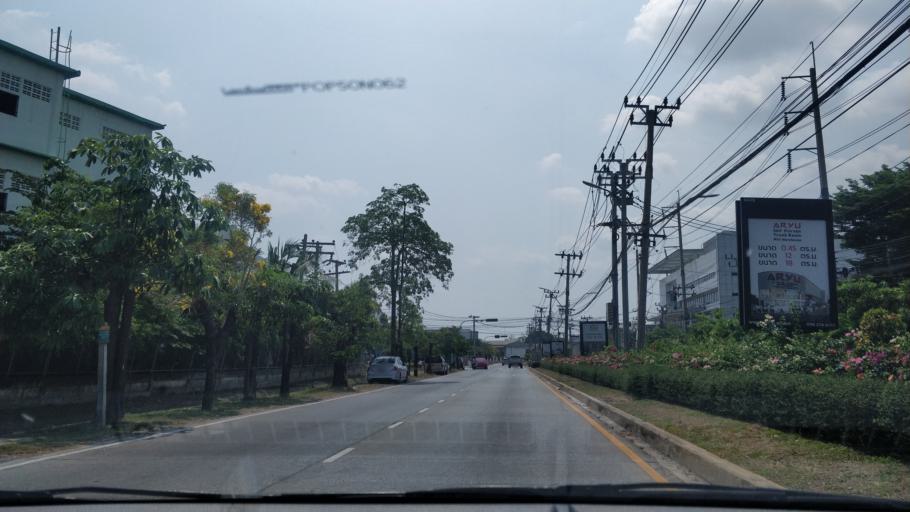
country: TH
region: Bangkok
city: Lat Krabang
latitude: 13.7578
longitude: 100.7910
